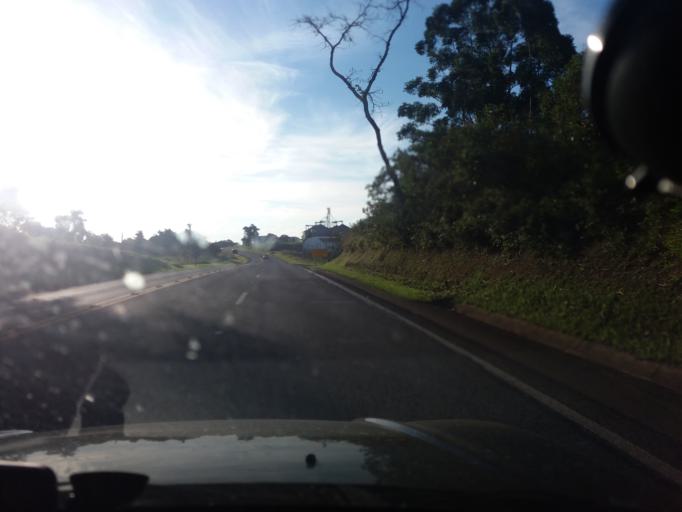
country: BR
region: Sao Paulo
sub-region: Buri
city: Buri
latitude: -23.9272
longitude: -48.6697
